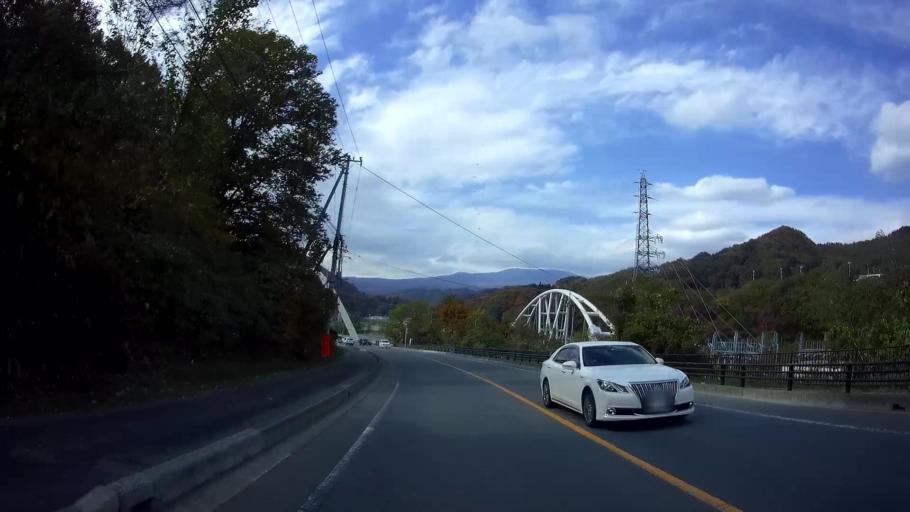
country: JP
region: Gunma
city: Nakanojomachi
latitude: 36.5430
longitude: 138.6579
